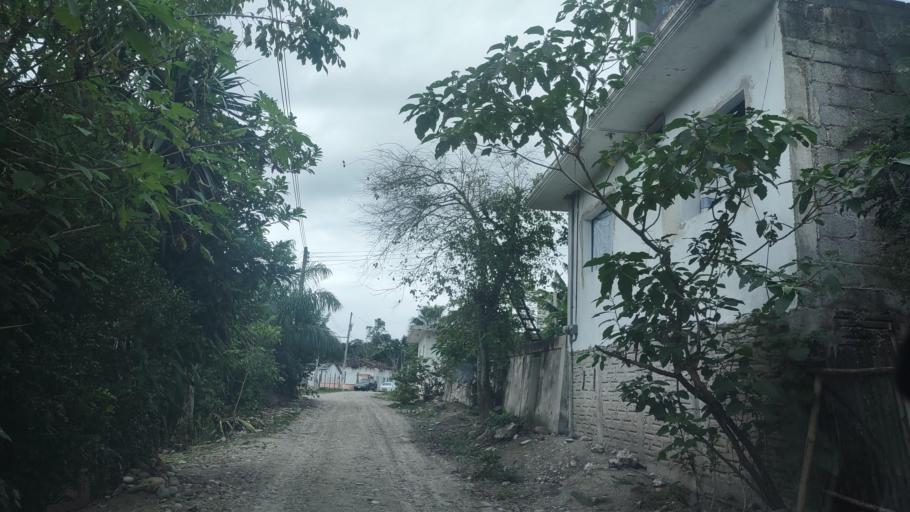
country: MX
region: Veracruz
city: Papantla de Olarte
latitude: 20.4360
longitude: -97.2619
